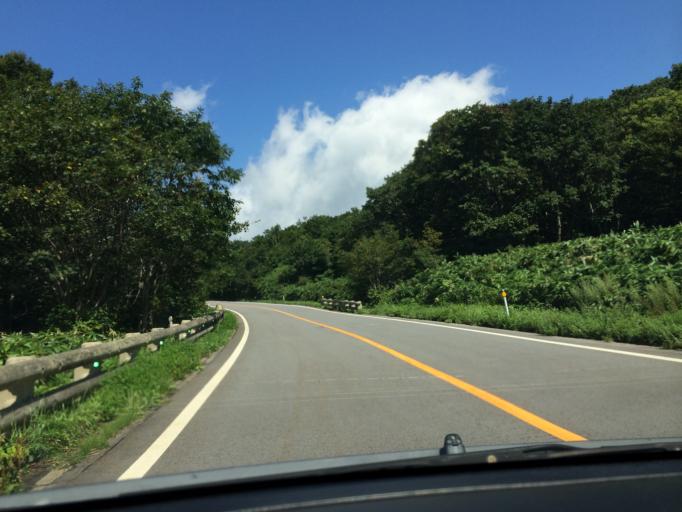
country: JP
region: Tottori
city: Kurayoshi
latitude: 35.3418
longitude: 133.5900
